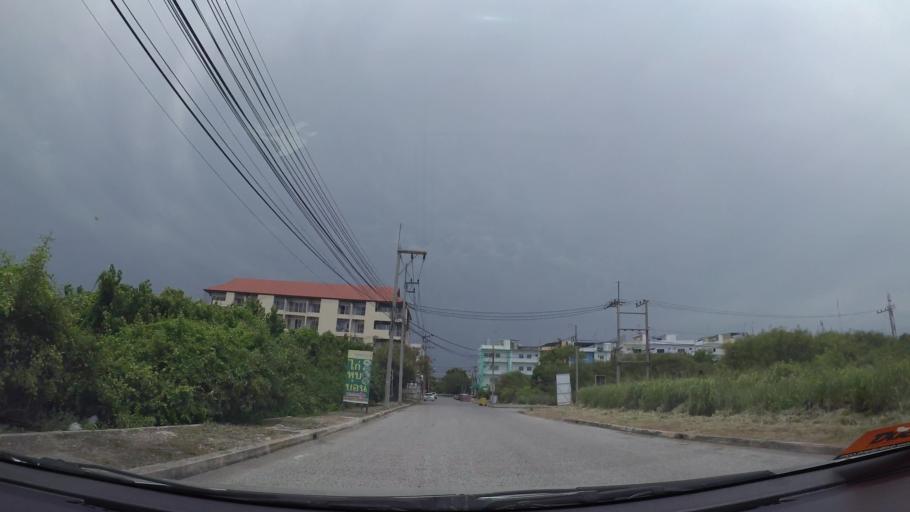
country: TH
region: Chon Buri
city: Chon Buri
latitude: 13.3404
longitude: 100.9563
